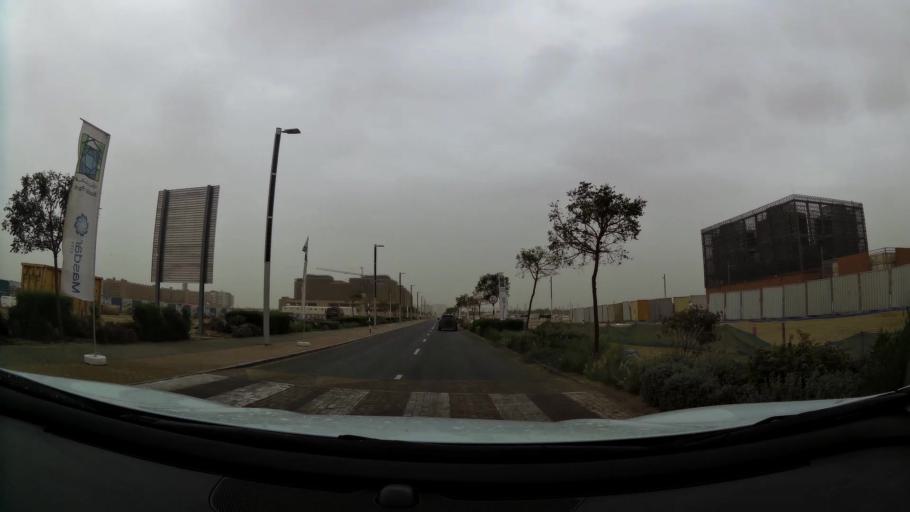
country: AE
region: Abu Dhabi
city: Abu Dhabi
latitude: 24.4334
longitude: 54.6246
